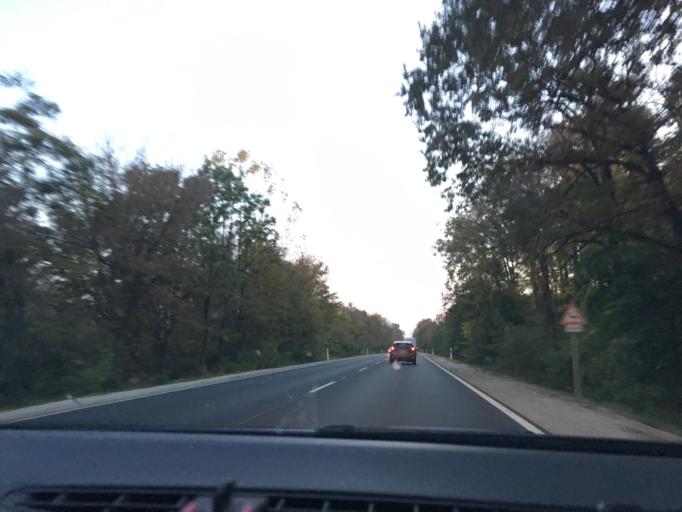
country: HU
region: Hajdu-Bihar
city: Debrecen
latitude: 47.5682
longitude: 21.6525
